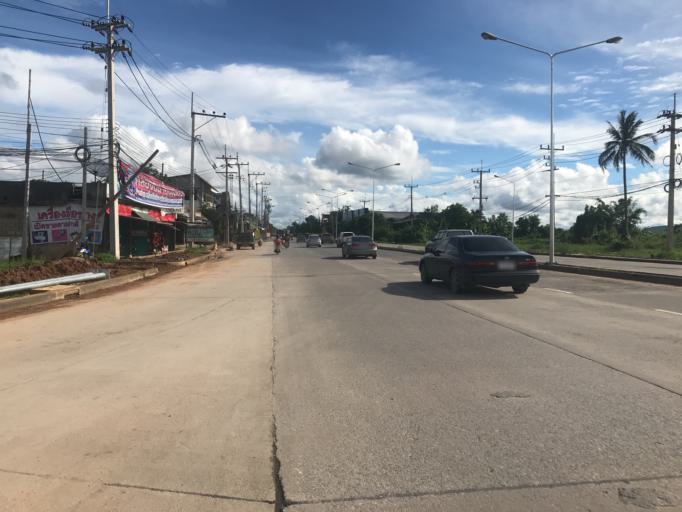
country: TH
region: Chiang Rai
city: Chiang Rai
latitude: 19.9593
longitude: 99.8531
